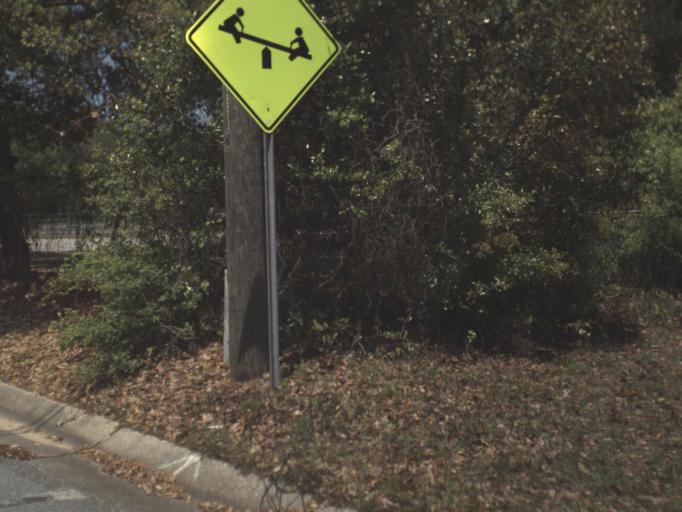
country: US
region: Florida
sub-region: Escambia County
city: Ferry Pass
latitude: 30.4948
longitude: -87.1653
